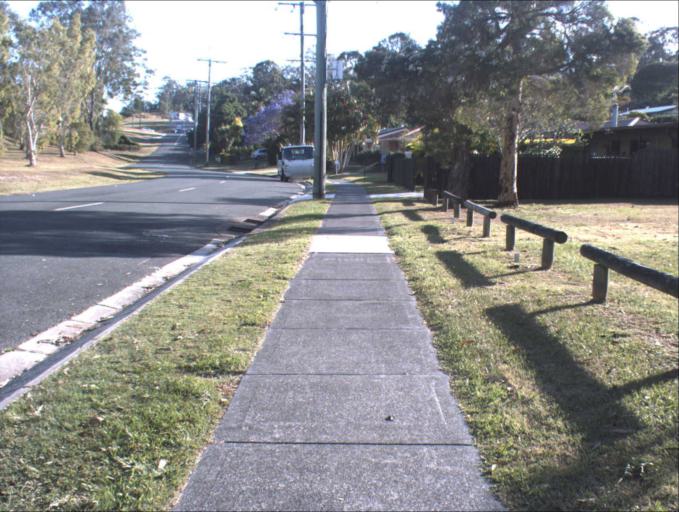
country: AU
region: Queensland
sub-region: Logan
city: Windaroo
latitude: -27.7244
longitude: 153.1935
